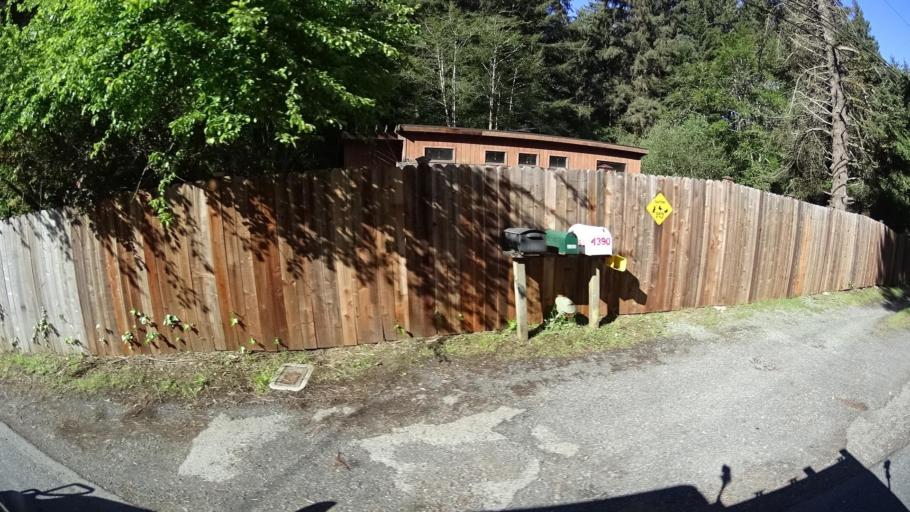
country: US
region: California
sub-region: Humboldt County
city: McKinleyville
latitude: 40.9839
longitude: -124.0991
